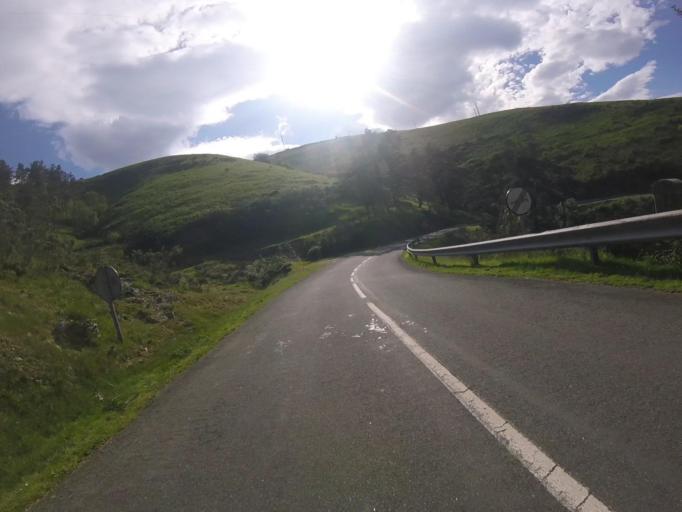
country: ES
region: Navarre
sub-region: Provincia de Navarra
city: Arano
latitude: 43.2449
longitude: -1.8457
